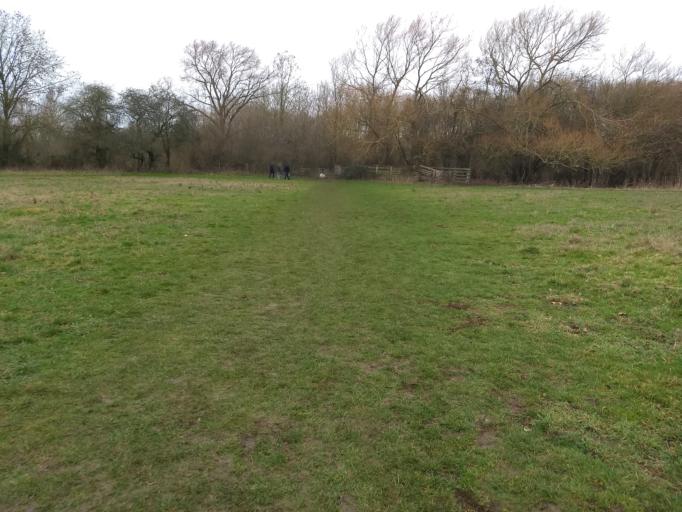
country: GB
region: England
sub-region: Bedford
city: Odell
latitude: 52.2057
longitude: -0.5897
